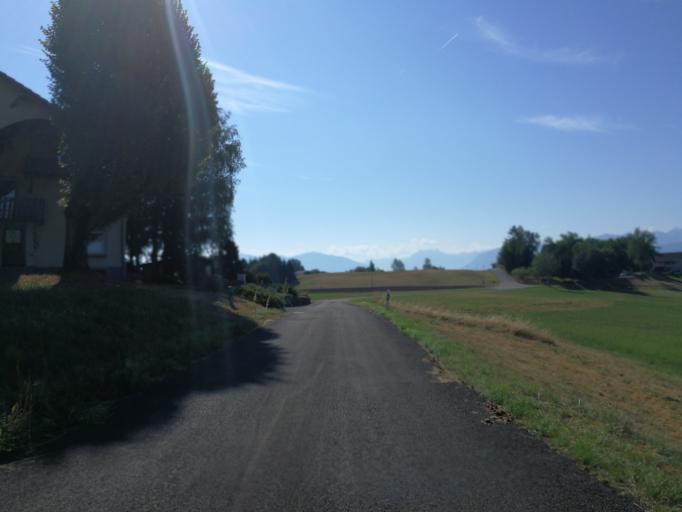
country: CH
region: Zurich
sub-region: Bezirk Hinwil
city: Durnten
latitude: 47.2719
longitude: 8.8335
